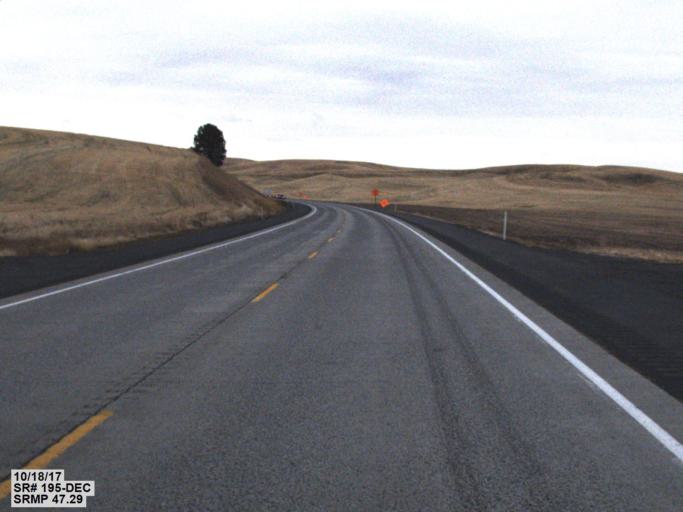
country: US
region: Washington
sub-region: Whitman County
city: Colfax
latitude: 46.9958
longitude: -117.3539
